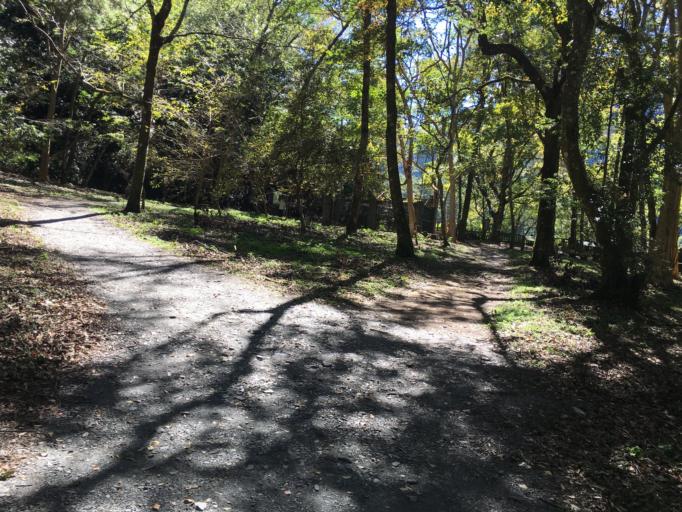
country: TW
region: Taiwan
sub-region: Nantou
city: Puli
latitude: 23.9464
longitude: 121.1904
